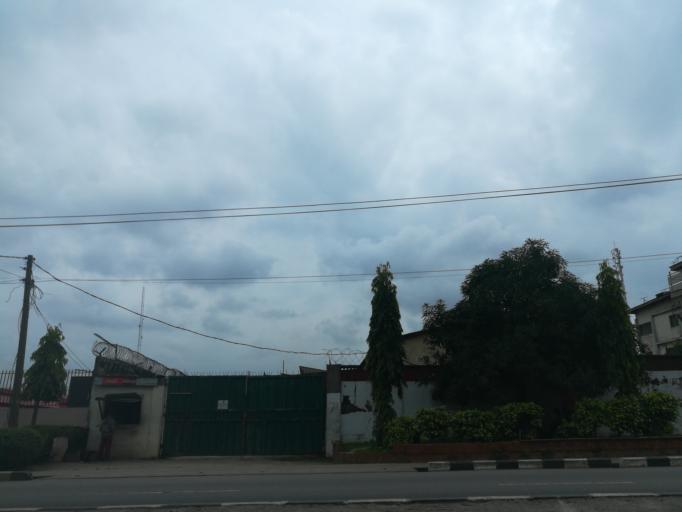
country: NG
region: Lagos
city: Ikeja
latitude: 6.6070
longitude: 3.3591
